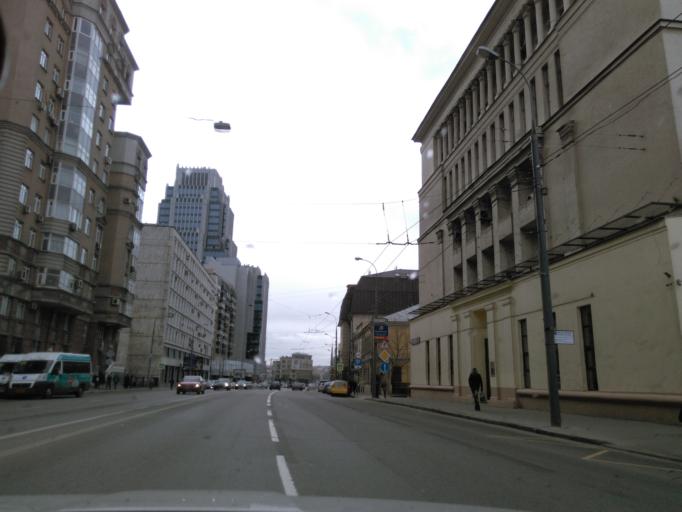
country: RU
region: Moscow
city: Mar'ina Roshcha
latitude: 55.7765
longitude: 37.6029
